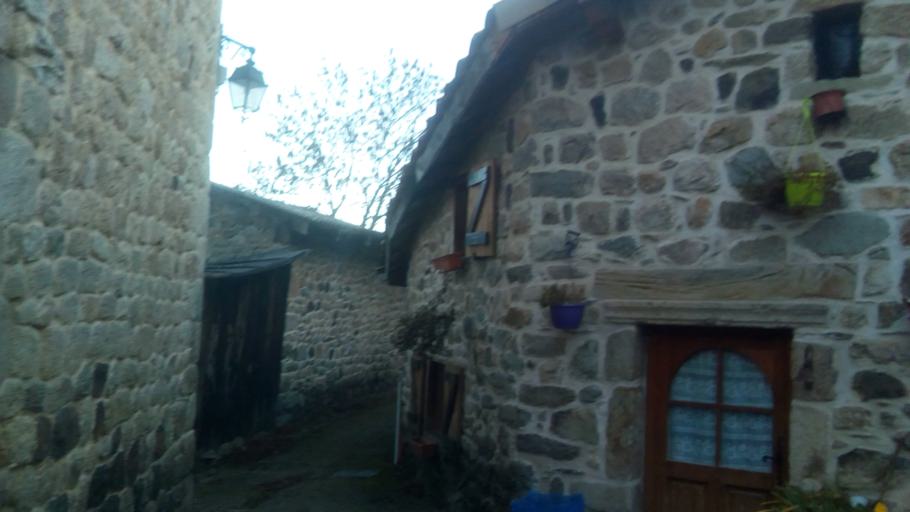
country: FR
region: Rhone-Alpes
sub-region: Departement de l'Ardeche
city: Le Chambon
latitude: 44.8786
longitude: 4.3311
